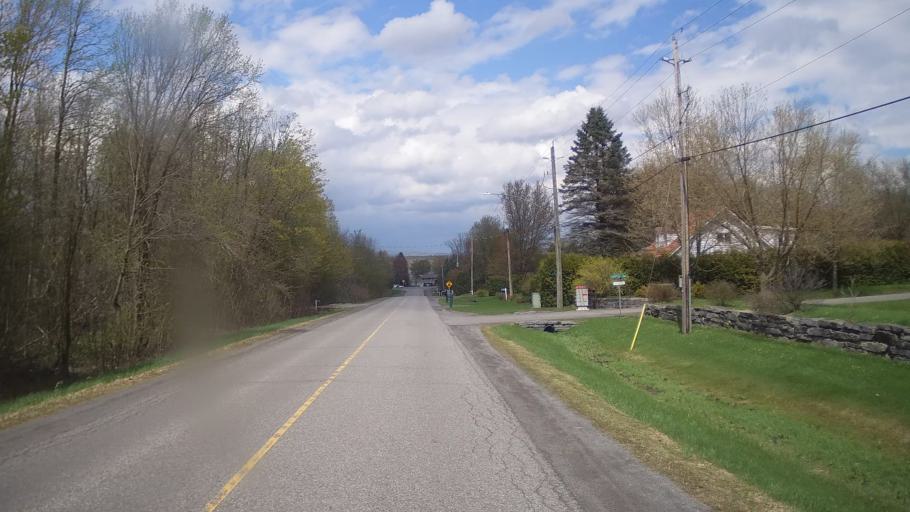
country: CA
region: Ontario
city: Hawkesbury
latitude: 45.5815
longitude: -74.5193
